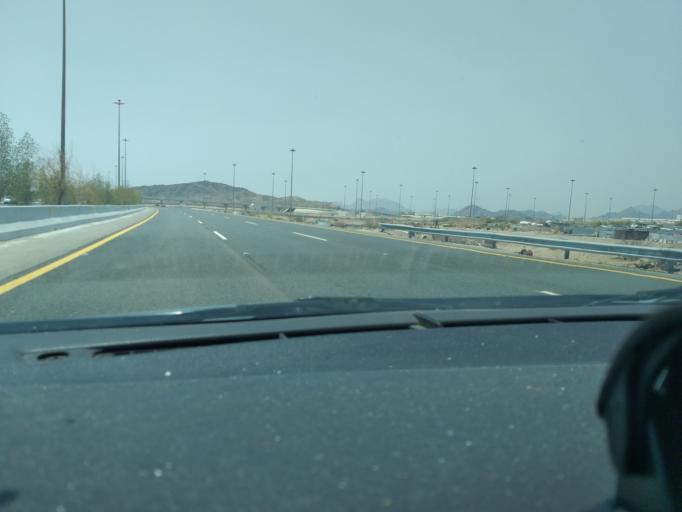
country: SA
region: Makkah
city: Mecca
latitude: 21.3297
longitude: 39.9932
